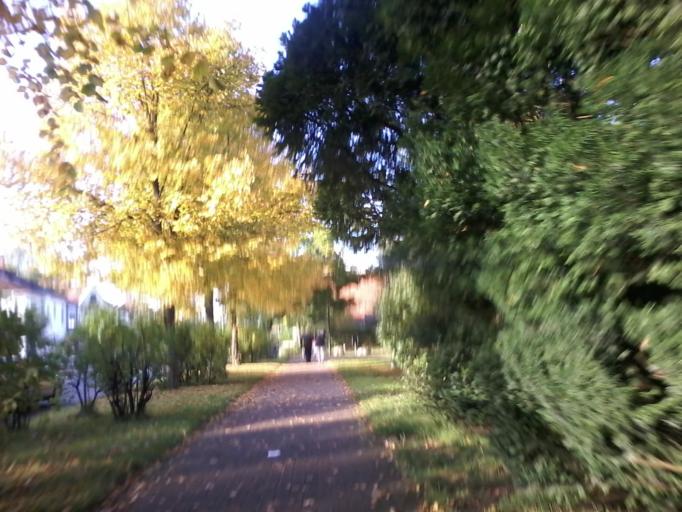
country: DE
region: Lower Saxony
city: Achim
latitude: 53.0137
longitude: 9.0330
